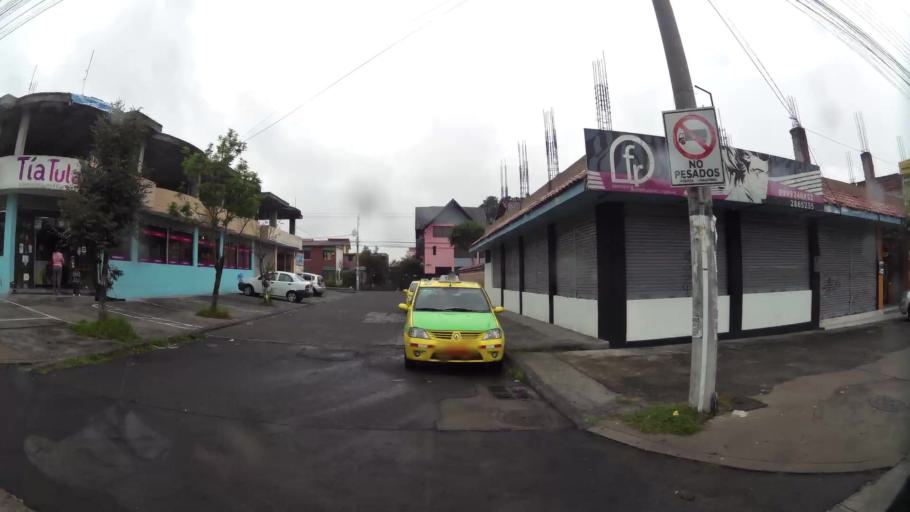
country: EC
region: Pichincha
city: Sangolqui
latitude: -0.2971
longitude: -78.4548
